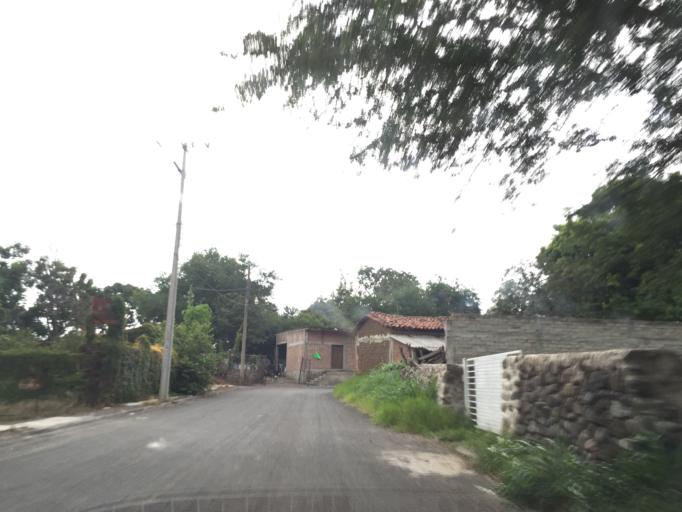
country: MX
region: Colima
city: Comala
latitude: 19.3379
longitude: -103.7761
